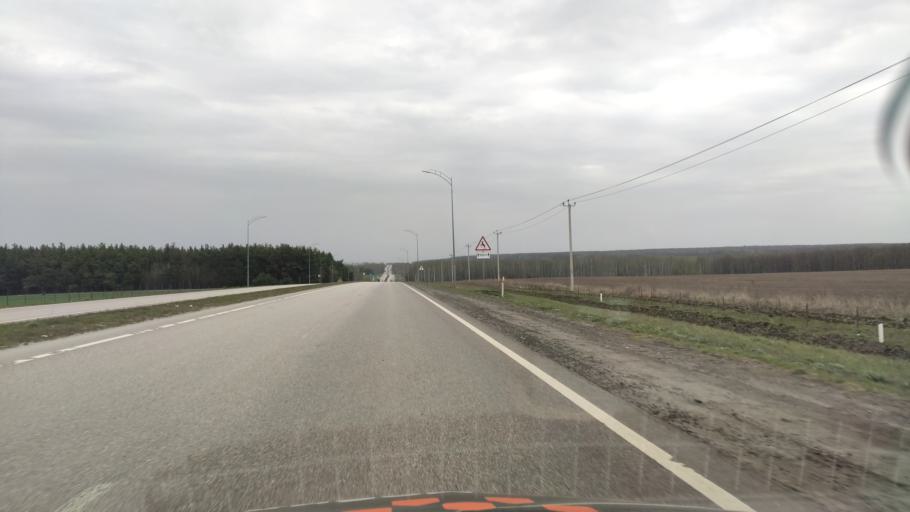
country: RU
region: Belgorod
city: Staryy Oskol
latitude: 51.3968
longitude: 37.8723
